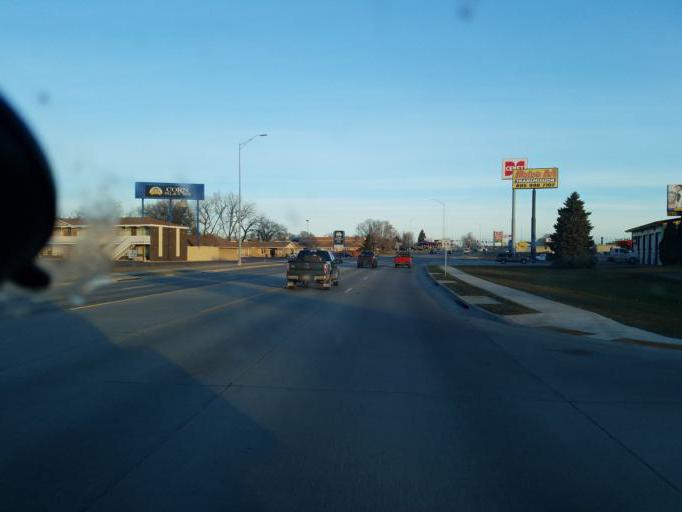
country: US
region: South Dakota
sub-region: Davison County
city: Mitchell
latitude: 43.6992
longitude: -98.0179
